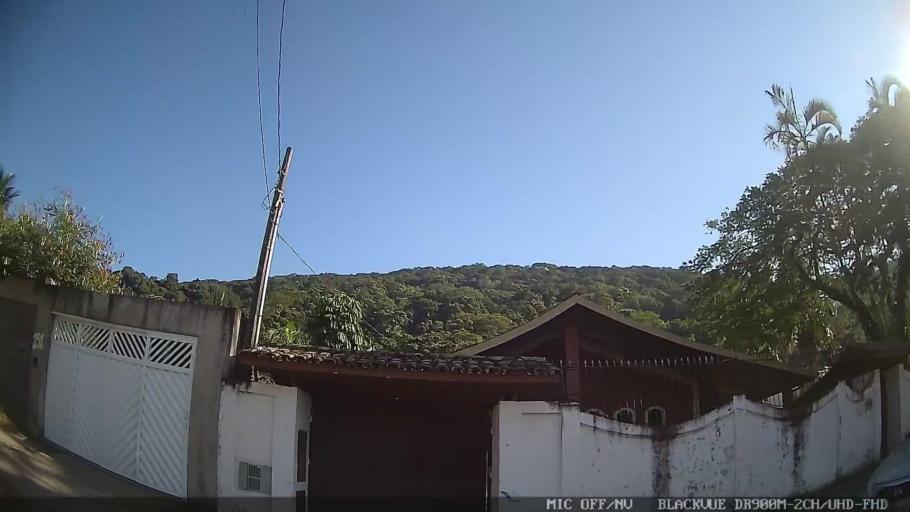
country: BR
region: Sao Paulo
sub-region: Guaruja
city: Guaruja
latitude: -24.0152
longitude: -46.2920
